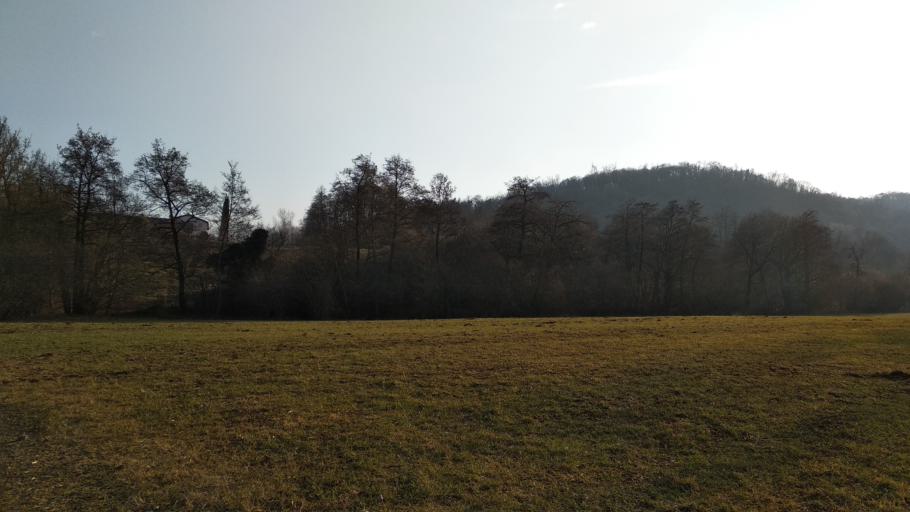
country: IT
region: Veneto
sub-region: Provincia di Vicenza
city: Monte di Malo
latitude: 45.6820
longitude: 11.3657
